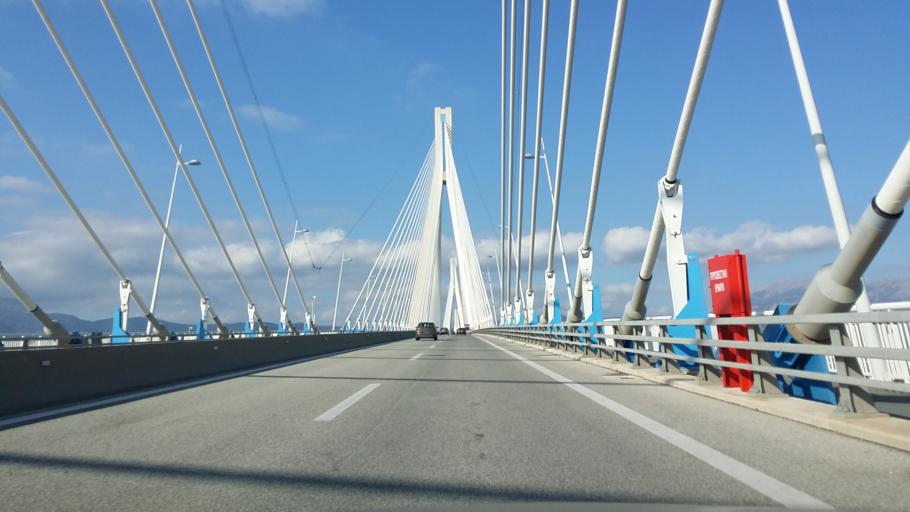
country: GR
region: West Greece
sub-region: Nomos Achaias
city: Rio
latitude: 38.3146
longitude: 21.7766
